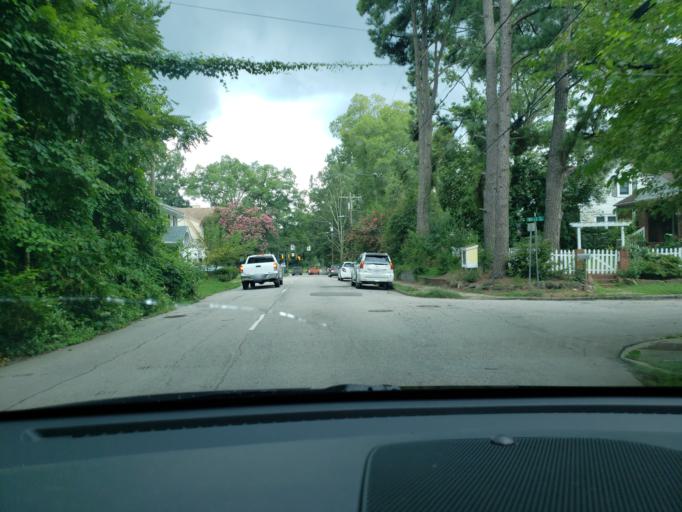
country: US
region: North Carolina
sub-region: Durham County
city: Durham
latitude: 35.9854
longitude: -78.9120
